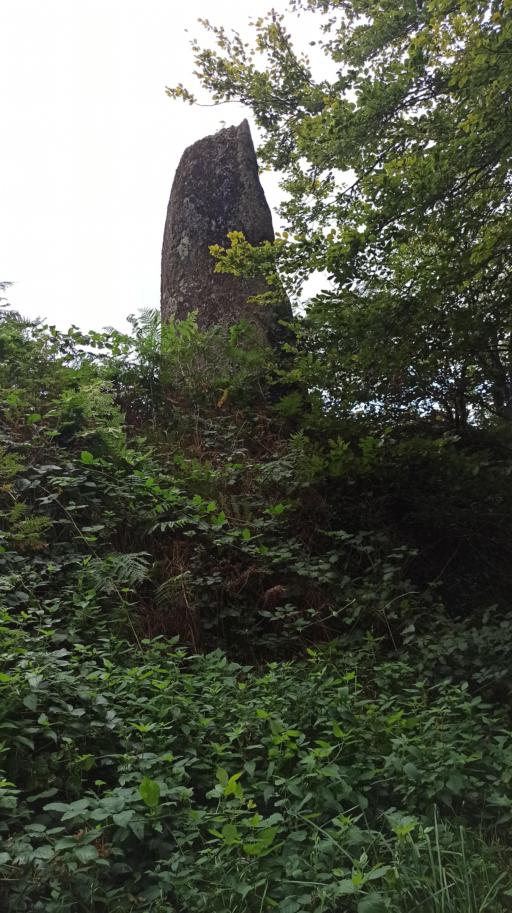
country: FR
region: Brittany
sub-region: Departement des Cotes-d'Armor
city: Bourbriac
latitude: 48.4318
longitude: -3.2322
